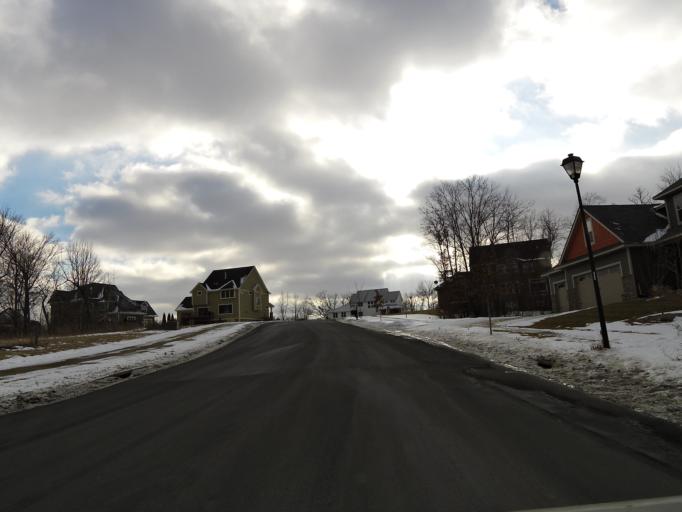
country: US
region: Minnesota
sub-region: Scott County
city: Prior Lake
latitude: 44.7419
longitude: -93.4518
